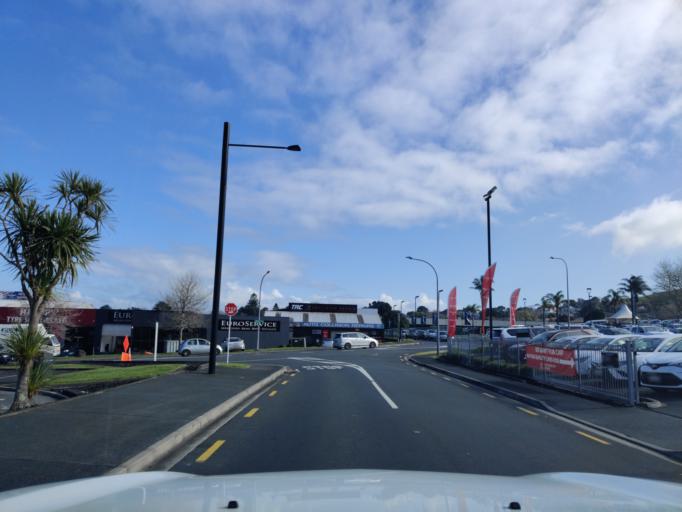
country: NZ
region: Auckland
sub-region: Auckland
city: Tamaki
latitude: -36.8976
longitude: 174.8485
